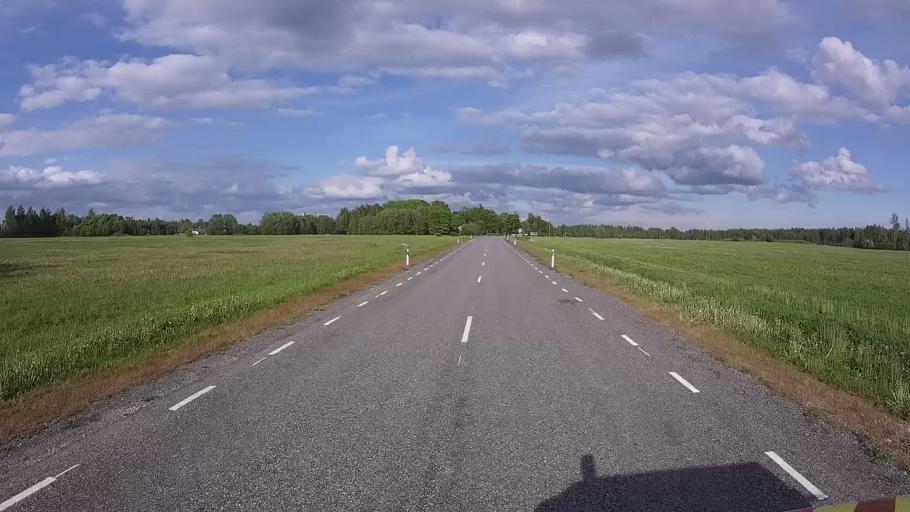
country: EE
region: Jogevamaa
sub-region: Mustvee linn
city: Mustvee
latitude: 59.0248
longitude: 27.0237
